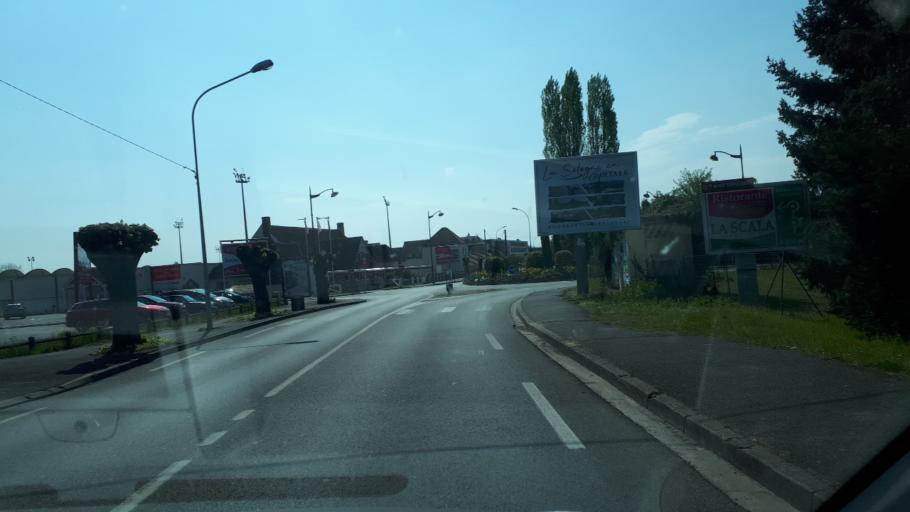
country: FR
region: Centre
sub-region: Departement du Loir-et-Cher
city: Romorantin-Lanthenay
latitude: 47.3720
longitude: 1.7378
